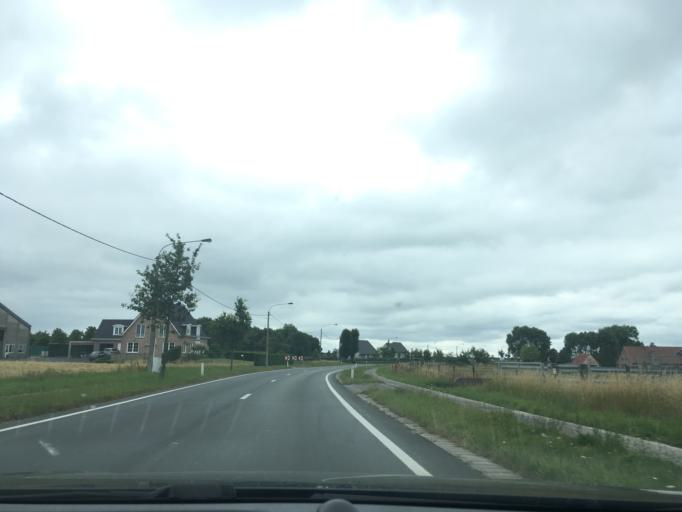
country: BE
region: Flanders
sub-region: Provincie West-Vlaanderen
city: Tielt
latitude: 51.0157
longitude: 3.3112
